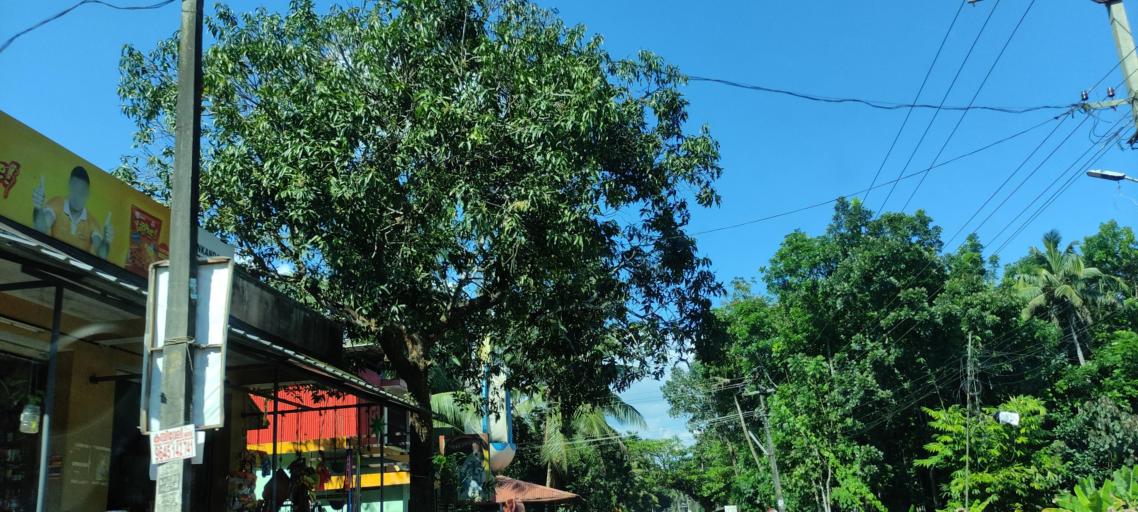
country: IN
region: Kerala
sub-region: Pattanamtitta
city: Adur
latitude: 9.1845
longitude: 76.7445
